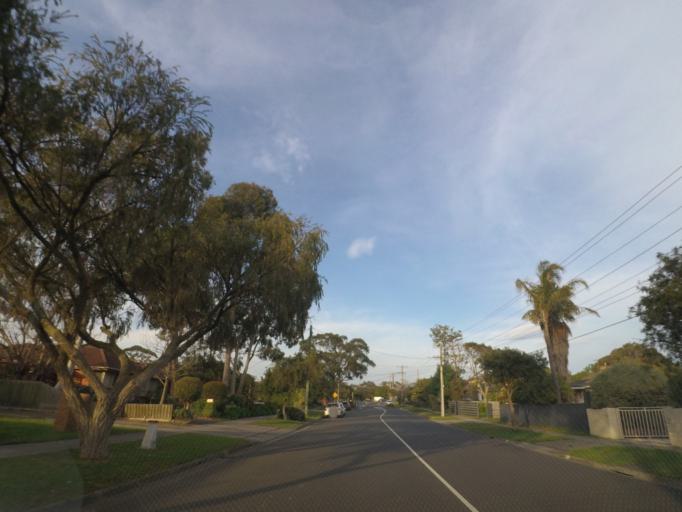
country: AU
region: Victoria
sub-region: Knox
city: Bayswater
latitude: -37.8618
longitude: 145.2503
